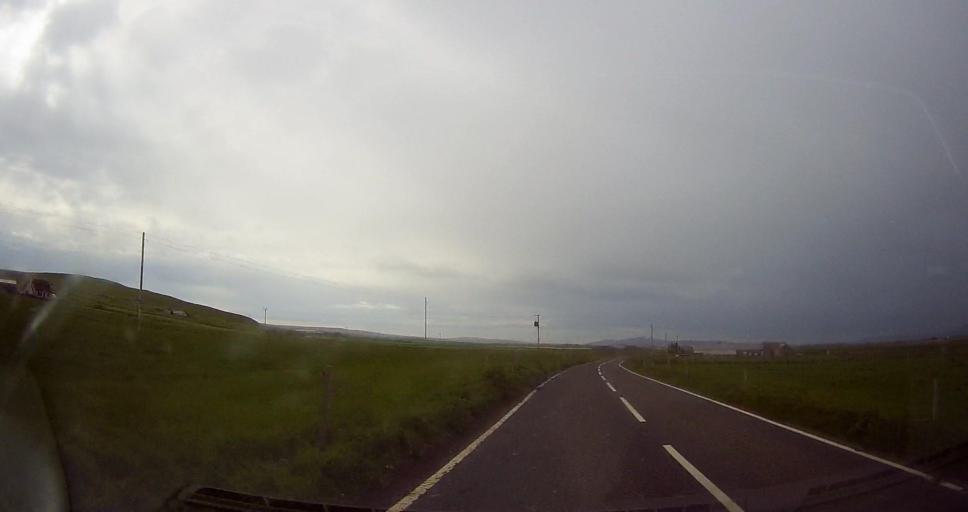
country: GB
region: Scotland
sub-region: Orkney Islands
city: Stromness
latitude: 59.0931
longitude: -3.2627
